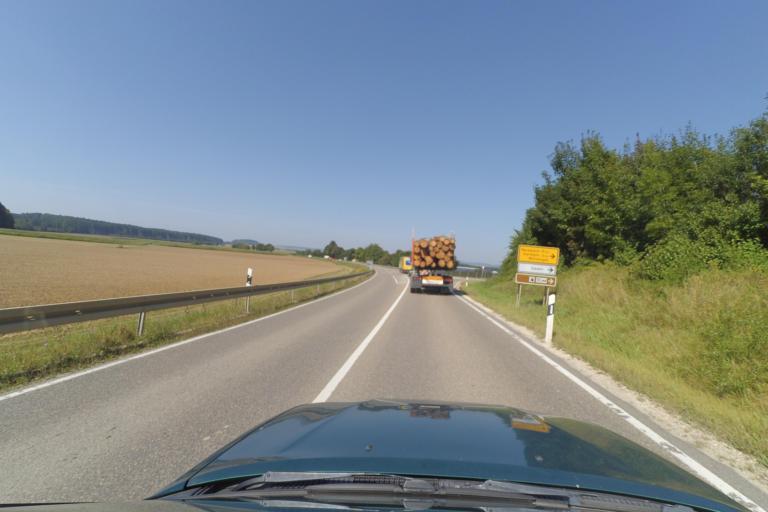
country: DE
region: Bavaria
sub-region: Swabia
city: Wittislingen
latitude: 48.6204
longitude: 10.4052
